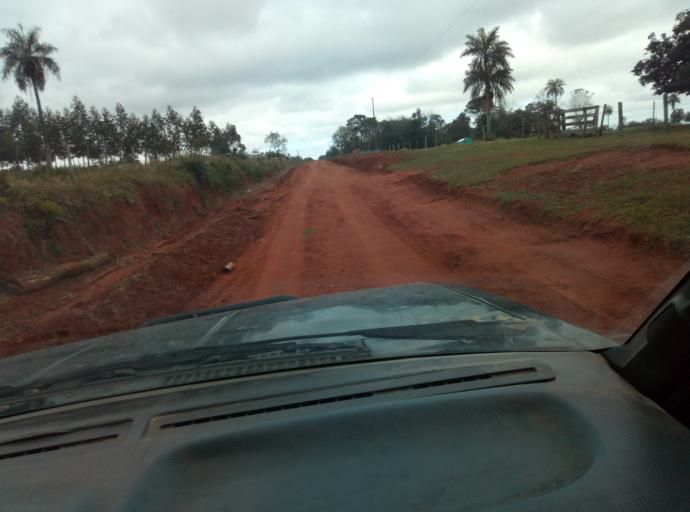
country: PY
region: Caaguazu
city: Doctor Cecilio Baez
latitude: -25.1472
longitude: -56.2905
